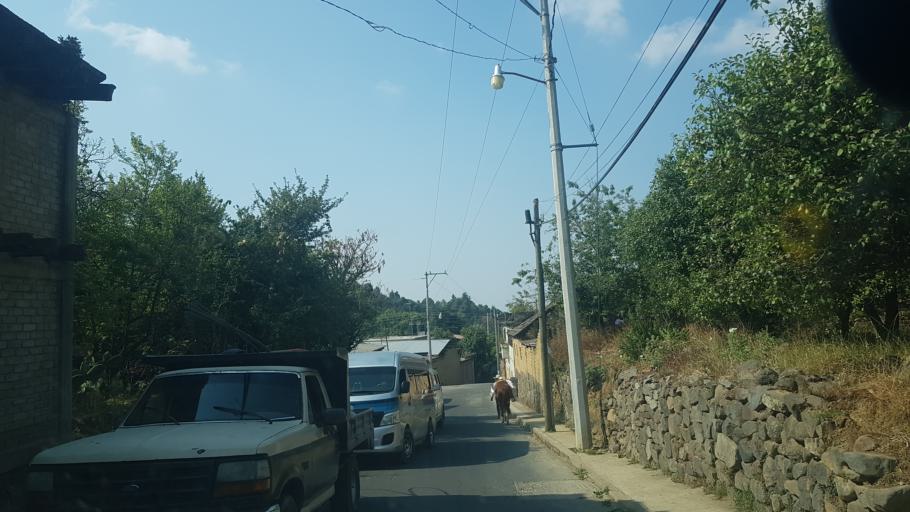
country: MX
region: Morelos
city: Hueyapan
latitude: 18.8887
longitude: -98.6808
